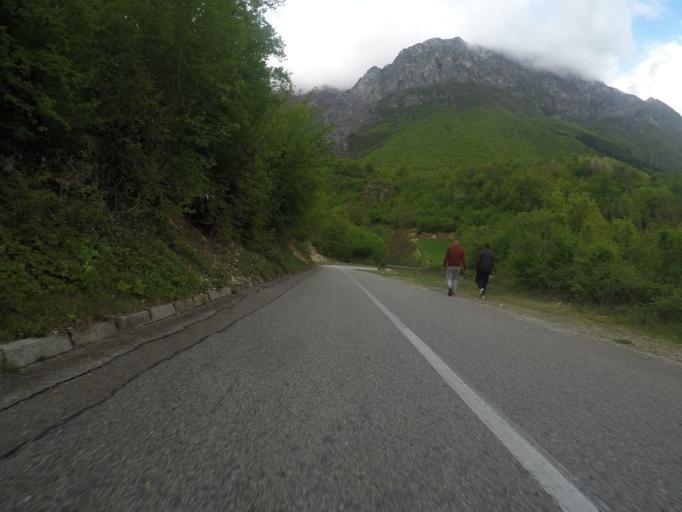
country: BA
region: Federation of Bosnia and Herzegovina
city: Siroki Brijeg
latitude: 43.5413
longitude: 17.5893
